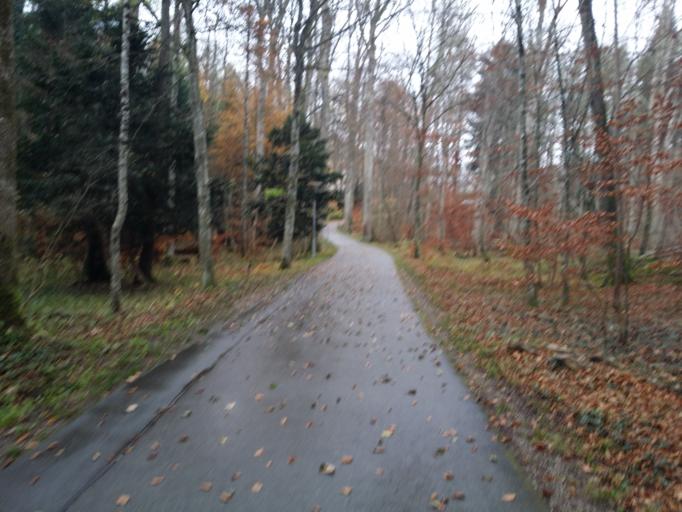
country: DE
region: Bavaria
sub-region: Upper Bavaria
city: Chiemsee
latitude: 47.8626
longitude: 12.4012
